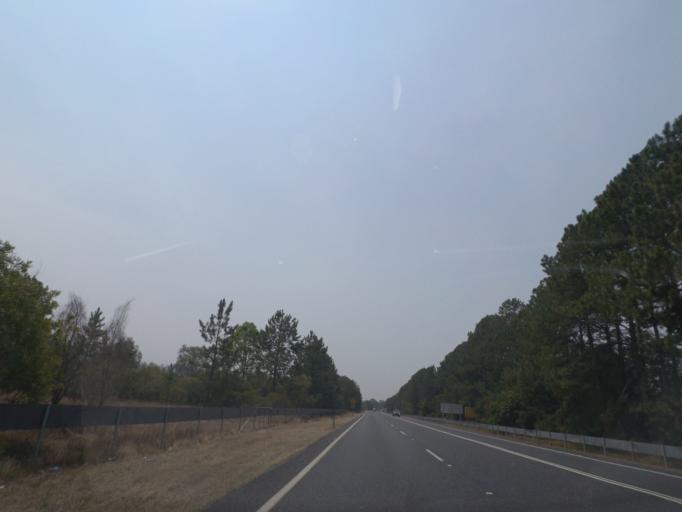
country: AU
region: New South Wales
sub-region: Ballina
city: Ballina
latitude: -28.9404
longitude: 153.4695
